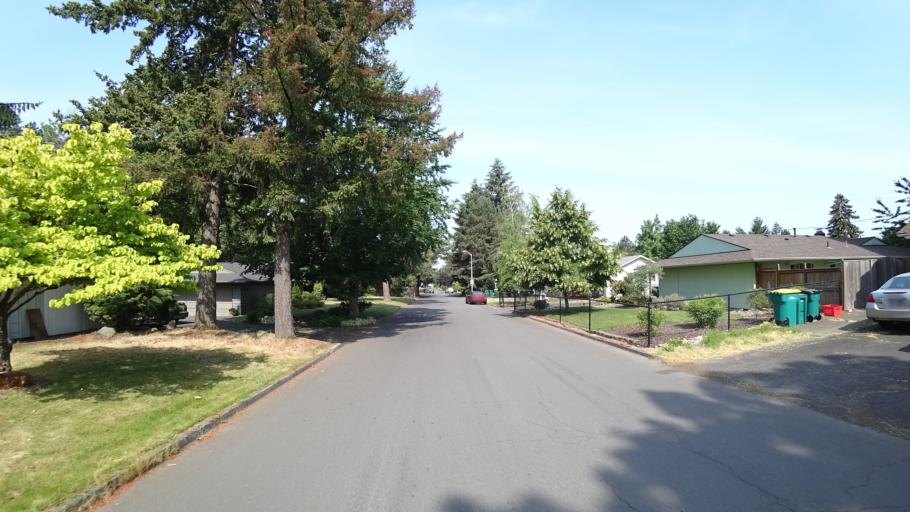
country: US
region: Oregon
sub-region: Washington County
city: Cedar Hills
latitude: 45.5035
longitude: -122.8188
